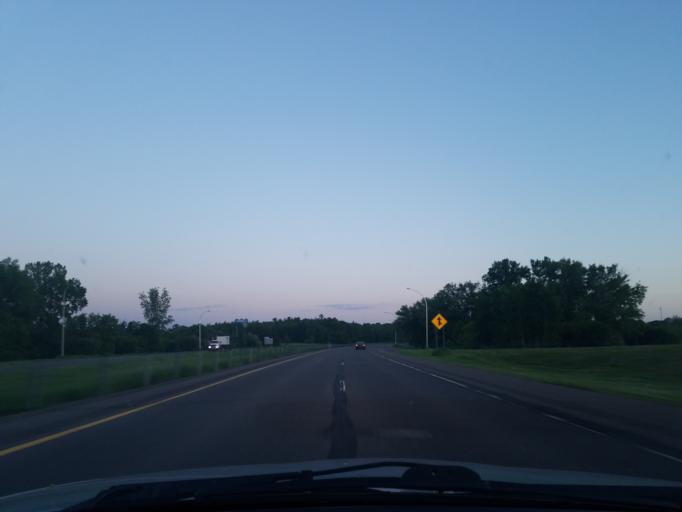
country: US
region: Minnesota
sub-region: Pine County
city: Pine City
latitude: 45.8206
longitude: -92.9837
